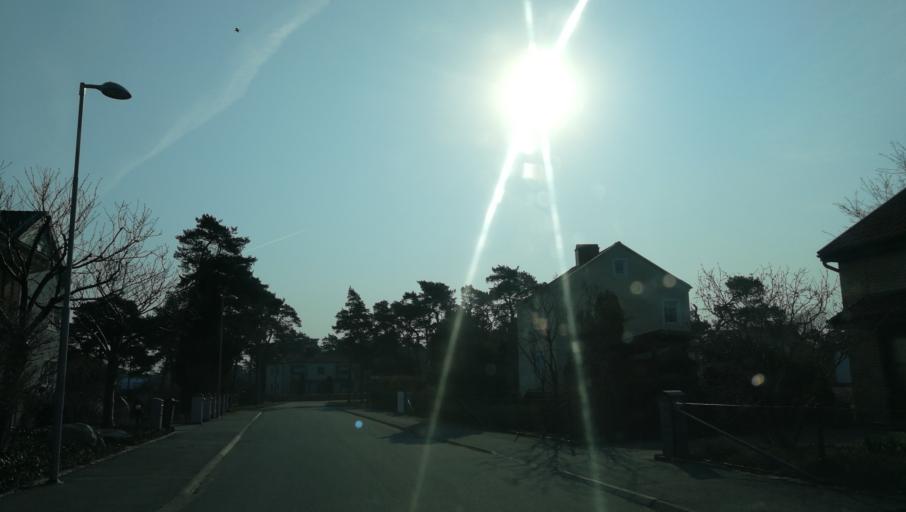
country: SE
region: Skane
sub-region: Ystads Kommun
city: Ystad
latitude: 55.4310
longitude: 13.8382
